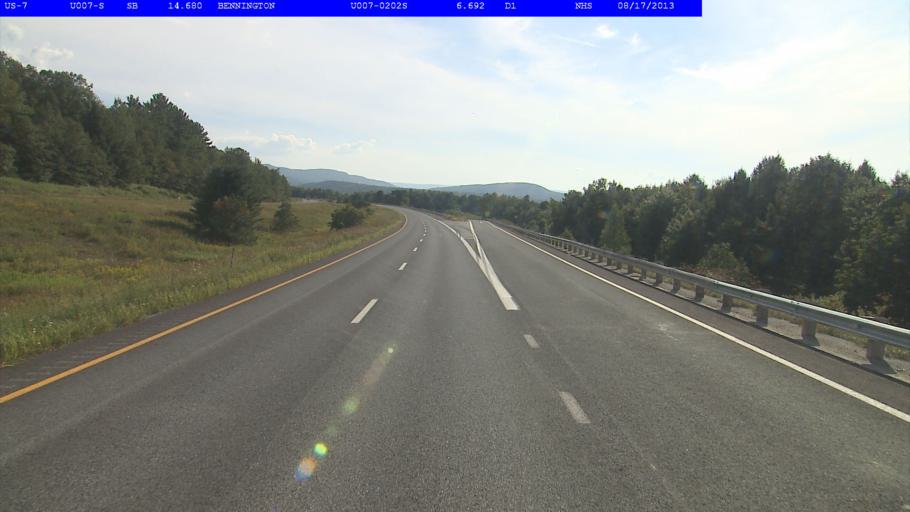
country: US
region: Vermont
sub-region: Bennington County
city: North Bennington
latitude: 42.9265
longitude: -73.2019
